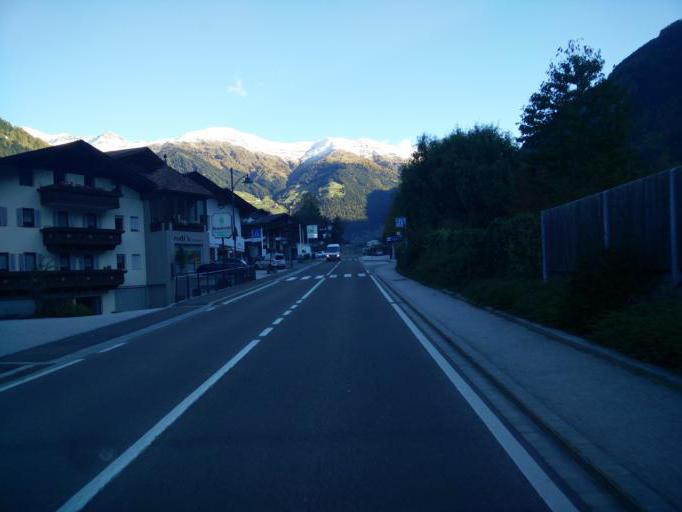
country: IT
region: Trentino-Alto Adige
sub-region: Bolzano
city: San Martino in Passiria
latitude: 46.7844
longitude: 11.2293
